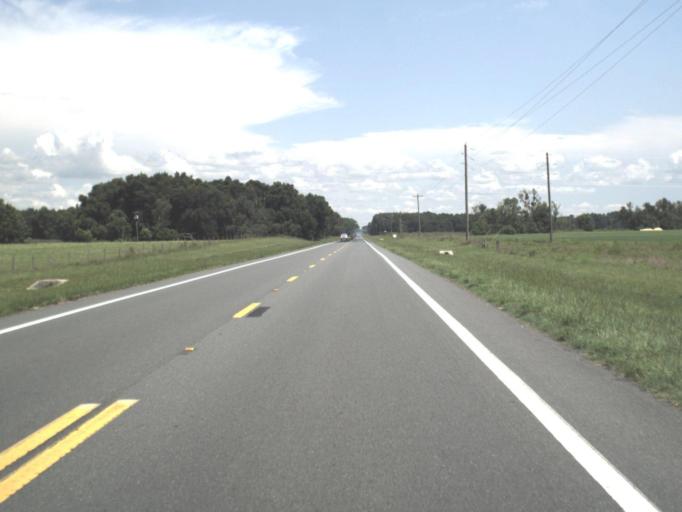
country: US
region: Florida
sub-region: Lafayette County
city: Mayo
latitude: 30.1101
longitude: -83.2520
